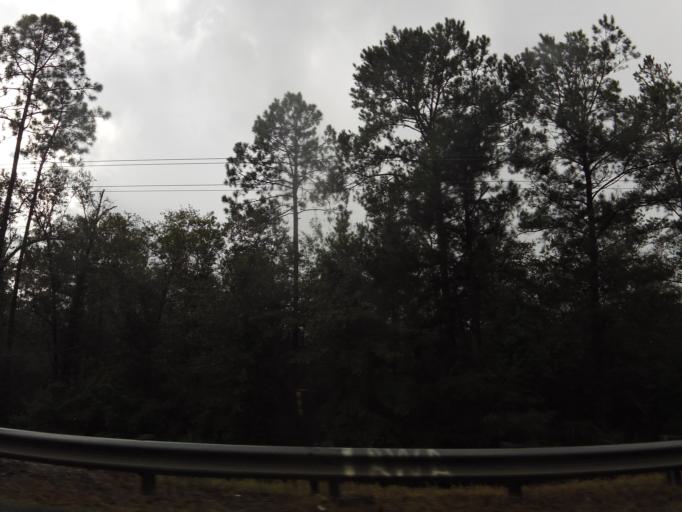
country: US
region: Florida
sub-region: Baker County
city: Macclenny
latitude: 30.3656
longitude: -82.1364
